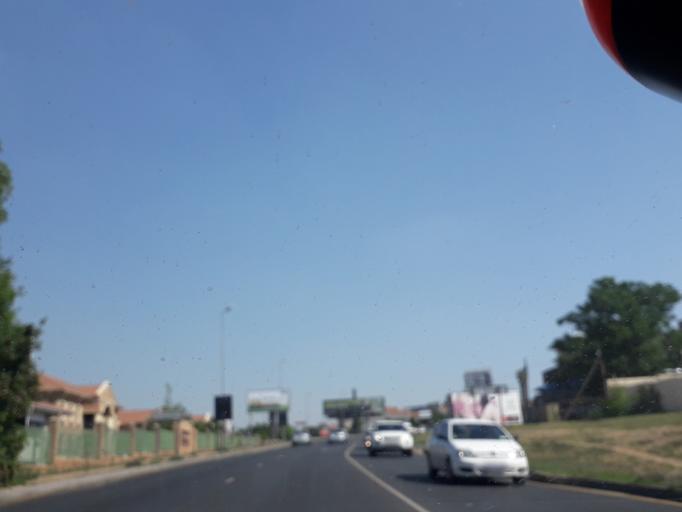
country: ZA
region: Gauteng
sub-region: City of Johannesburg Metropolitan Municipality
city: Modderfontein
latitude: -26.0731
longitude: 28.0646
